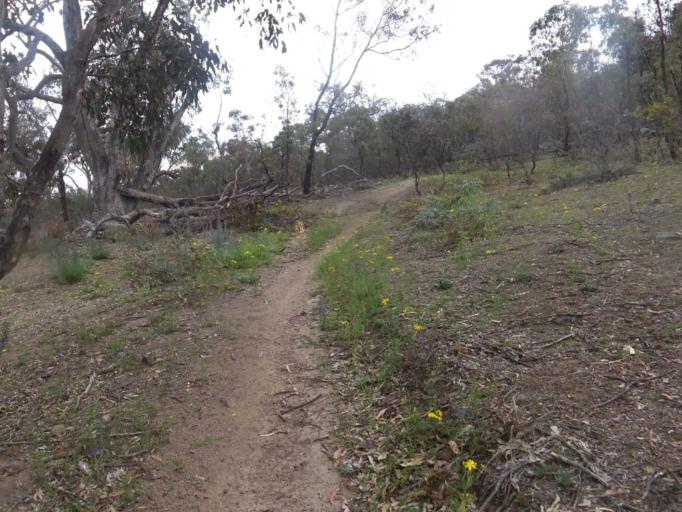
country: AU
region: Australian Capital Territory
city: Forrest
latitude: -35.3558
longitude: 149.1240
